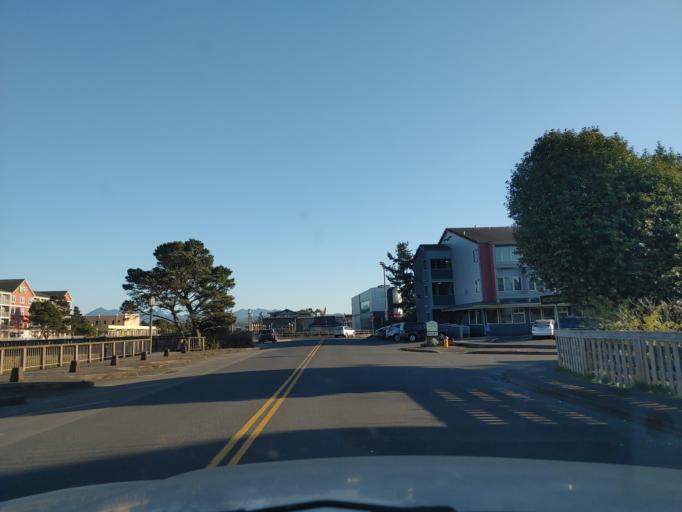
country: US
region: Oregon
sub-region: Clatsop County
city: Seaside
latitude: 45.9953
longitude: -123.9247
